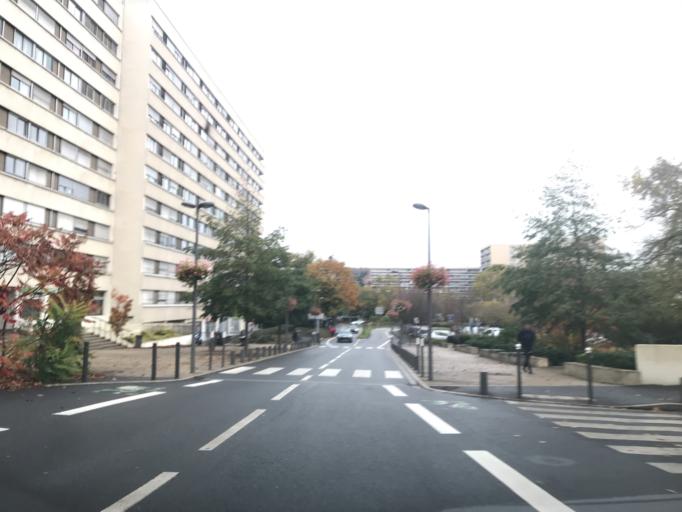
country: FR
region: Ile-de-France
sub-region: Departement de l'Essonne
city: Verrieres-le-Buisson
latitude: 48.7347
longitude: 2.2632
